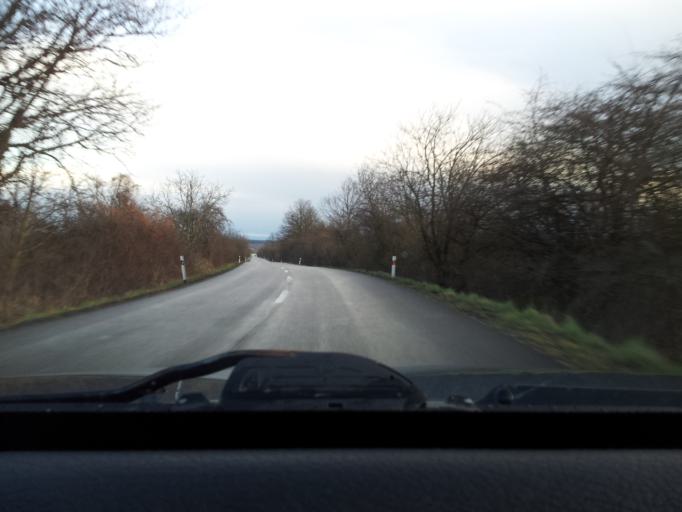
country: SK
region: Nitriansky
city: Tlmace
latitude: 48.3407
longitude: 18.4864
